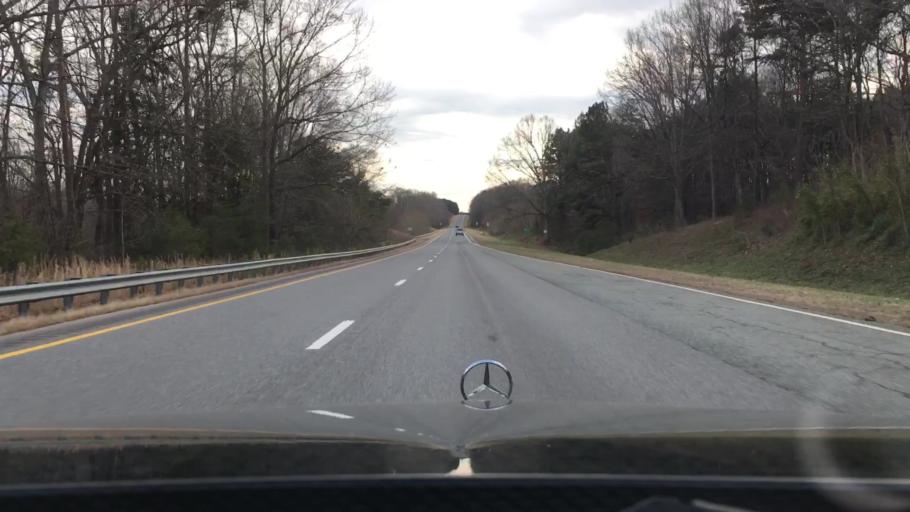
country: US
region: Virginia
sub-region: Pittsylvania County
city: Gretna
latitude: 36.9486
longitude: -79.3787
